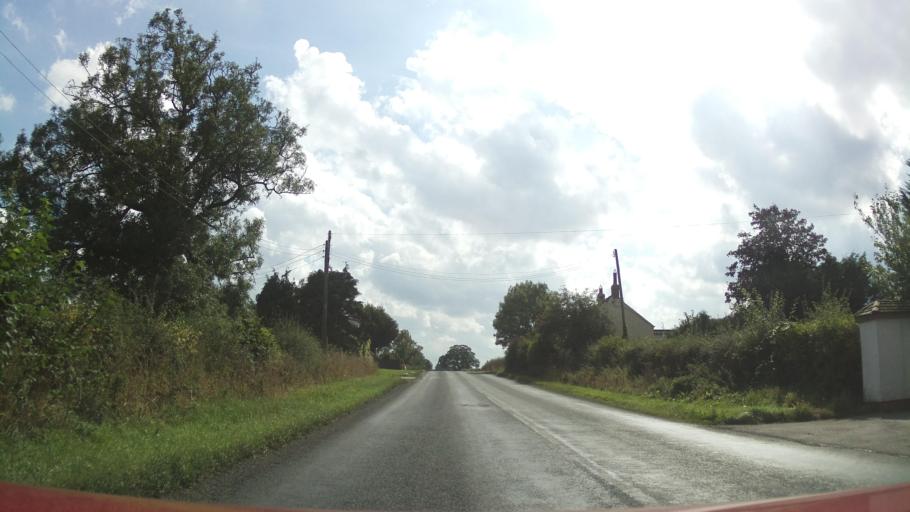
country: GB
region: England
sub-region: Darlington
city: High Coniscliffe
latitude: 54.5157
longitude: -1.6715
